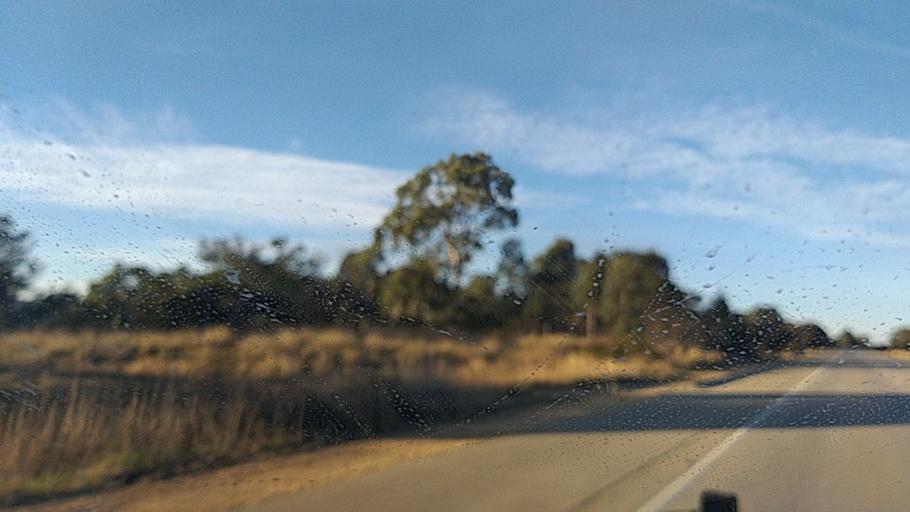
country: AU
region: New South Wales
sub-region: Yass Valley
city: Gundaroo
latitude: -35.1295
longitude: 149.3419
